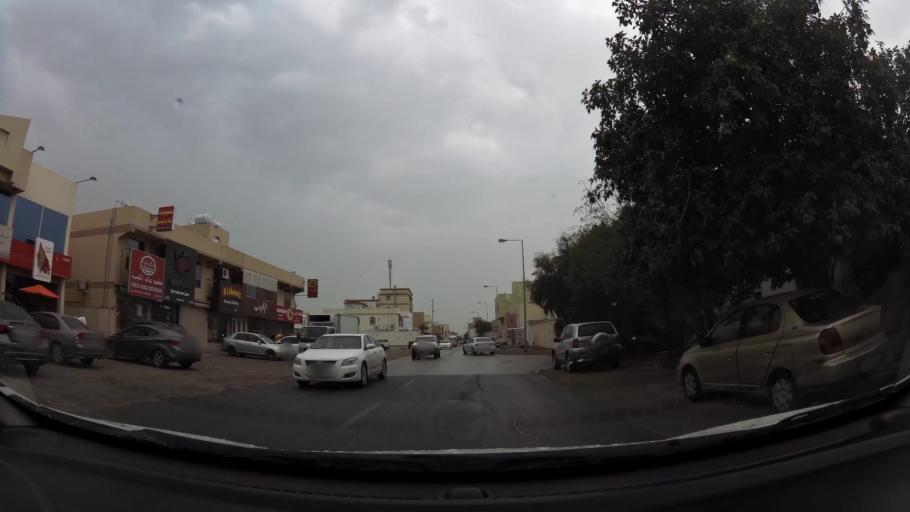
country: BH
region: Northern
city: Madinat `Isa
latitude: 26.1640
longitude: 50.5710
